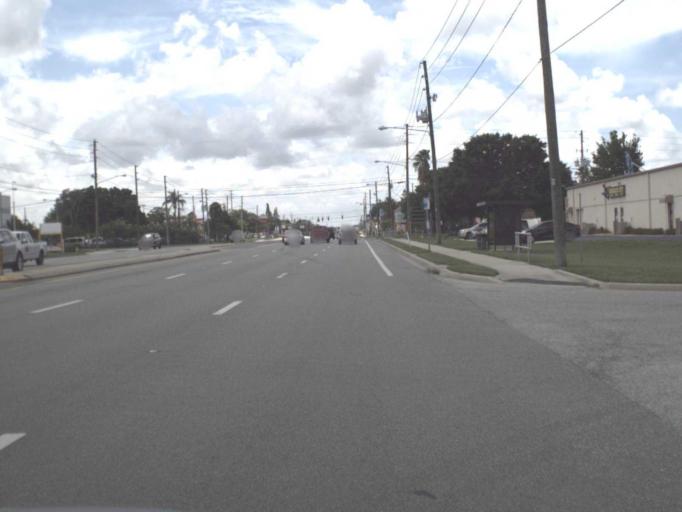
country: US
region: Florida
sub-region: Pinellas County
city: Pinellas Park
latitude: 27.8748
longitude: -82.7004
